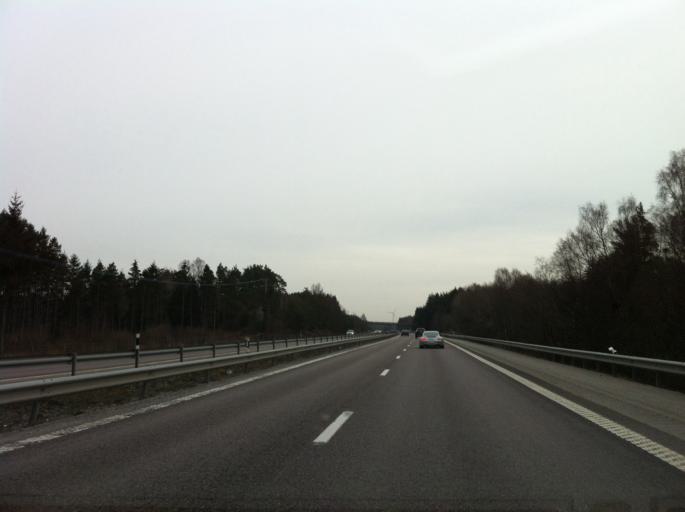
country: SE
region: Vaestra Goetaland
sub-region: Stenungsunds Kommun
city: Stora Hoga
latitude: 57.9944
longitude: 11.8421
